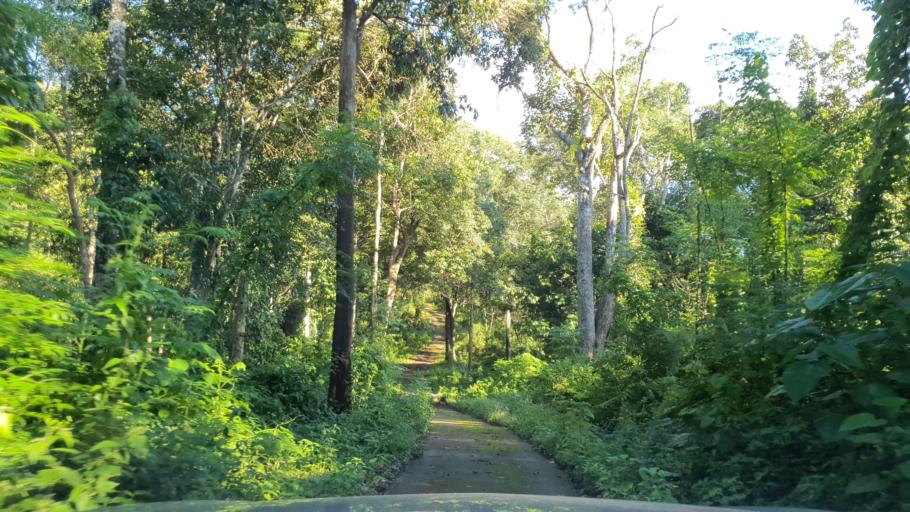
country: TH
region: Chiang Mai
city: Mae On
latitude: 18.8145
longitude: 99.3532
